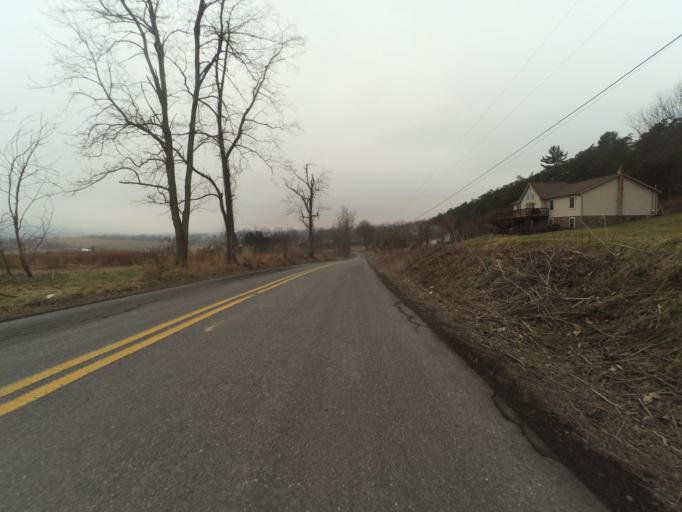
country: US
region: Pennsylvania
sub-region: Centre County
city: Centre Hall
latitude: 40.8191
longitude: -77.6110
